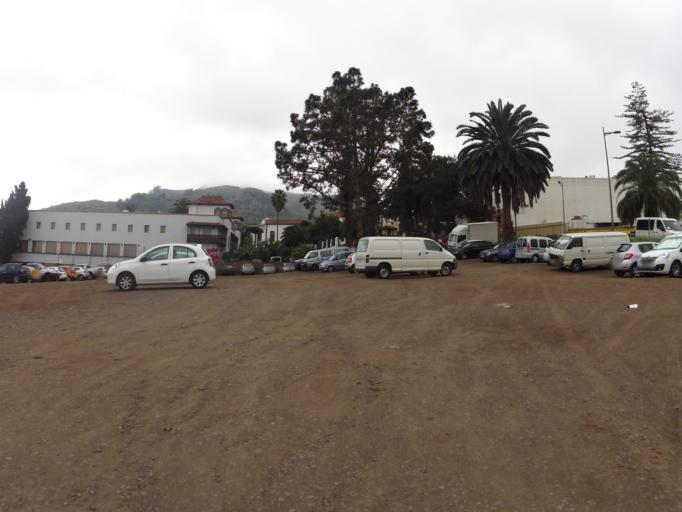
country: ES
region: Canary Islands
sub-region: Provincia de Las Palmas
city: Teror
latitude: 28.0615
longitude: -15.5454
